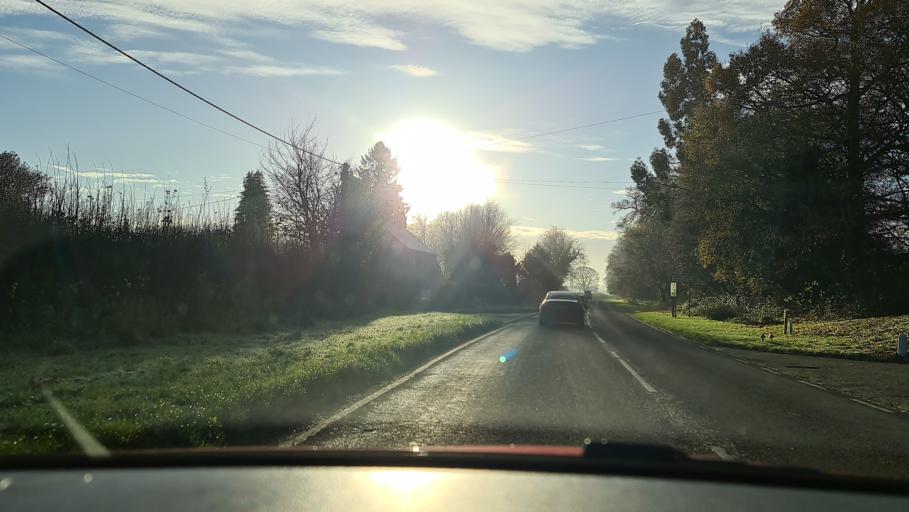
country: GB
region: England
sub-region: Buckinghamshire
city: Wendover
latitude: 51.7329
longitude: -0.7284
